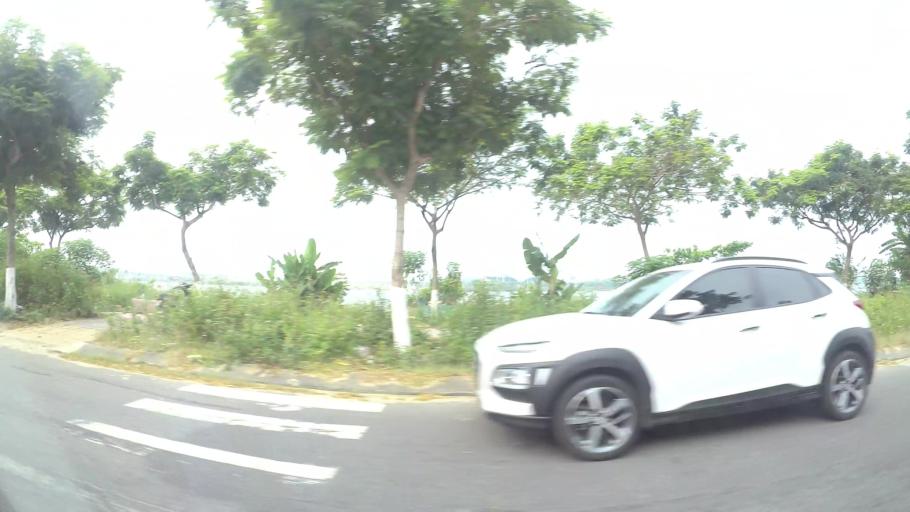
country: VN
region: Da Nang
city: Son Tra
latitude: 16.0389
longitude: 108.2372
